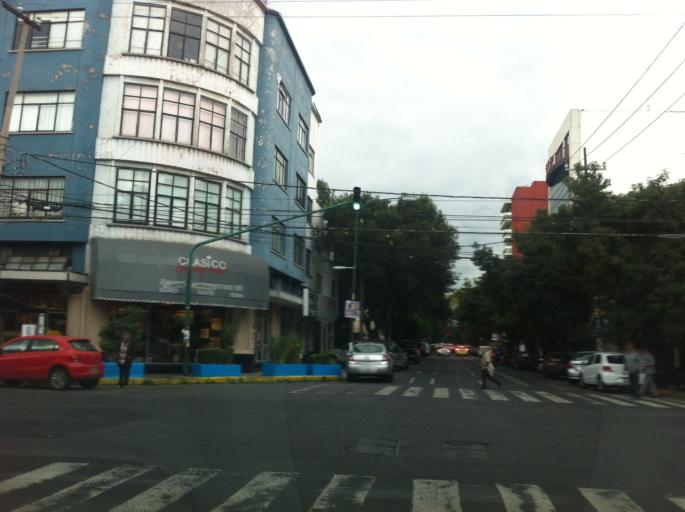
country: MX
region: Mexico City
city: Colonia del Valle
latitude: 19.3895
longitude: -99.1650
